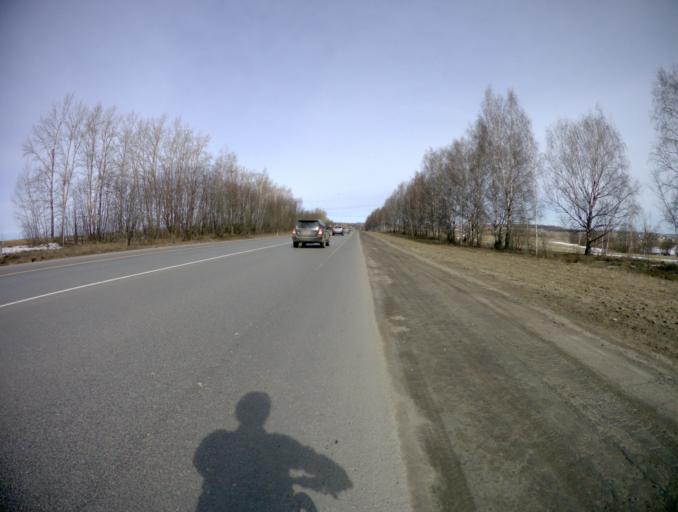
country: RU
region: Vladimir
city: Vladimir
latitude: 56.1848
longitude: 40.4485
